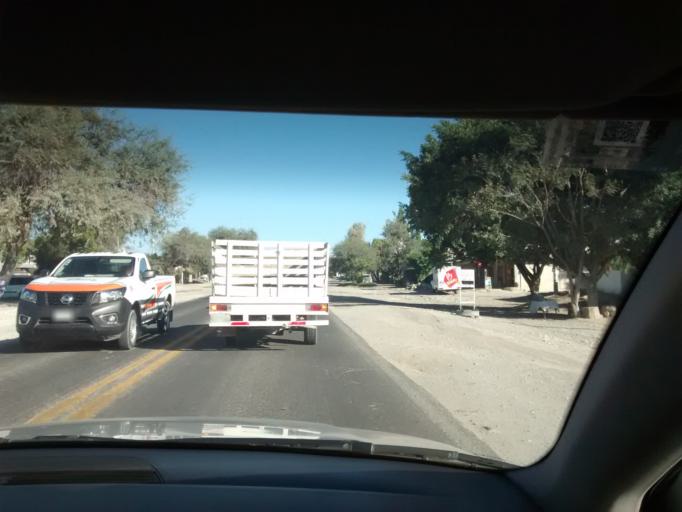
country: MX
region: Puebla
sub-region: Tehuacan
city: Magdalena Cuayucatepec
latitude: 18.5101
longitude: -97.4909
